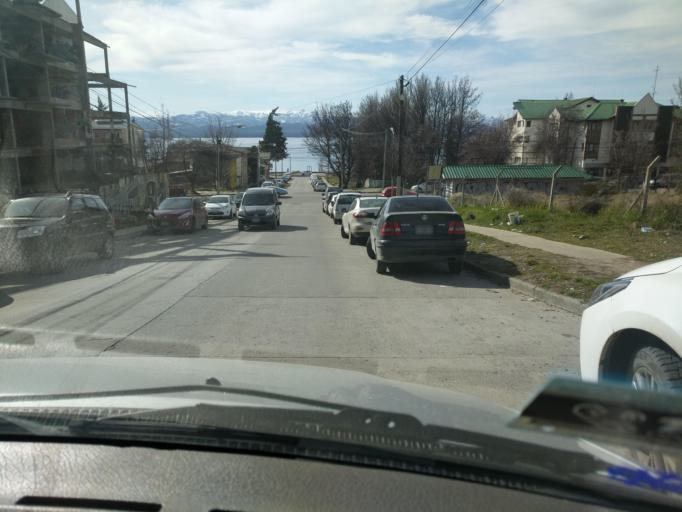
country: AR
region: Rio Negro
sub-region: Departamento de Bariloche
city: San Carlos de Bariloche
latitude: -41.1346
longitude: -71.2941
